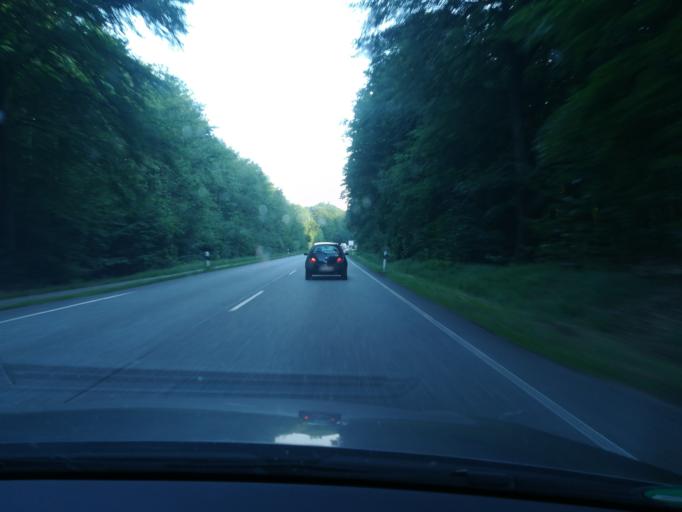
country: DE
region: Schleswig-Holstein
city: Kasseburg
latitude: 53.5388
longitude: 10.4249
